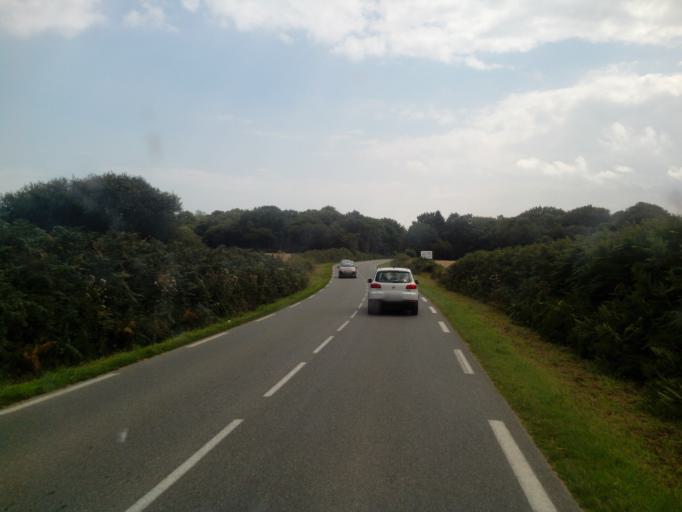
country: FR
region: Brittany
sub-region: Departement des Cotes-d'Armor
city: Plouha
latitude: 48.7037
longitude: -2.9508
